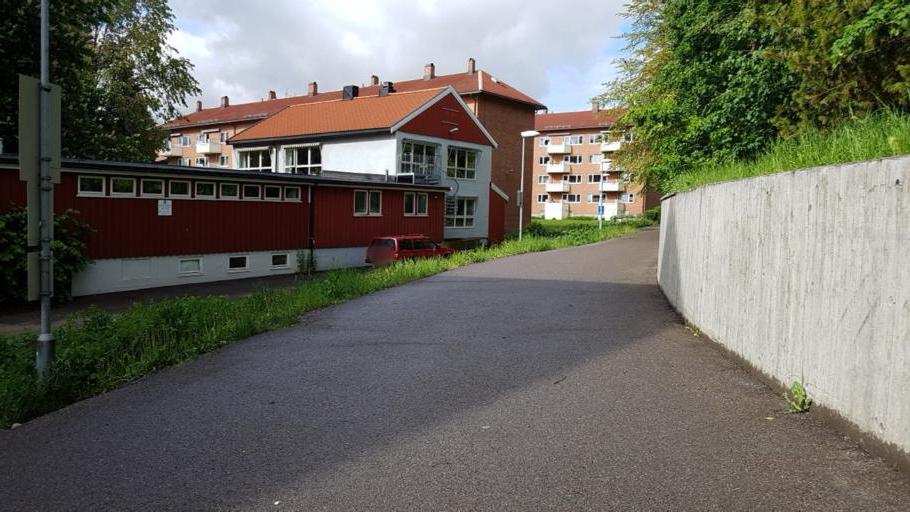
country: NO
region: Oslo
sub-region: Oslo
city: Oslo
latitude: 59.9362
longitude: 10.7778
